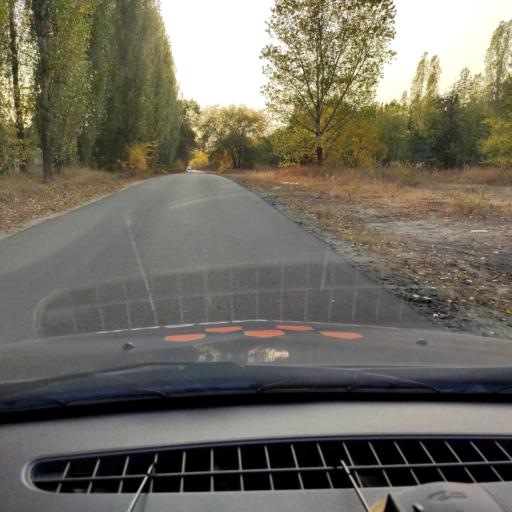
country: RU
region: Voronezj
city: Pridonskoy
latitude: 51.6644
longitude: 39.1163
